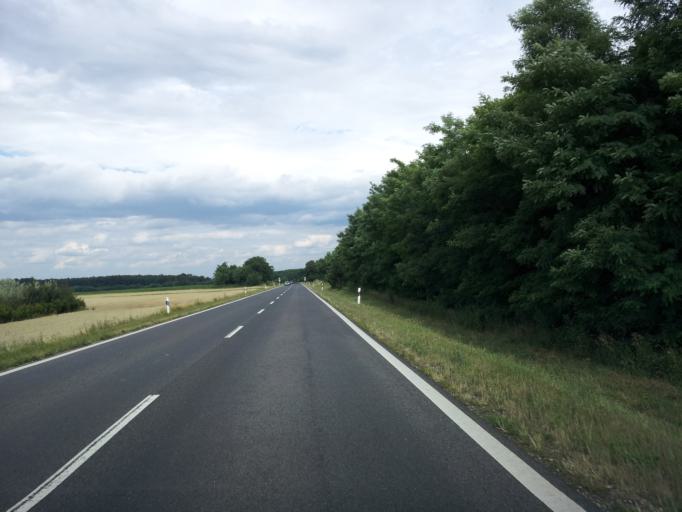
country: HU
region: Vas
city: Janoshaza
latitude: 47.0994
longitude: 17.0766
